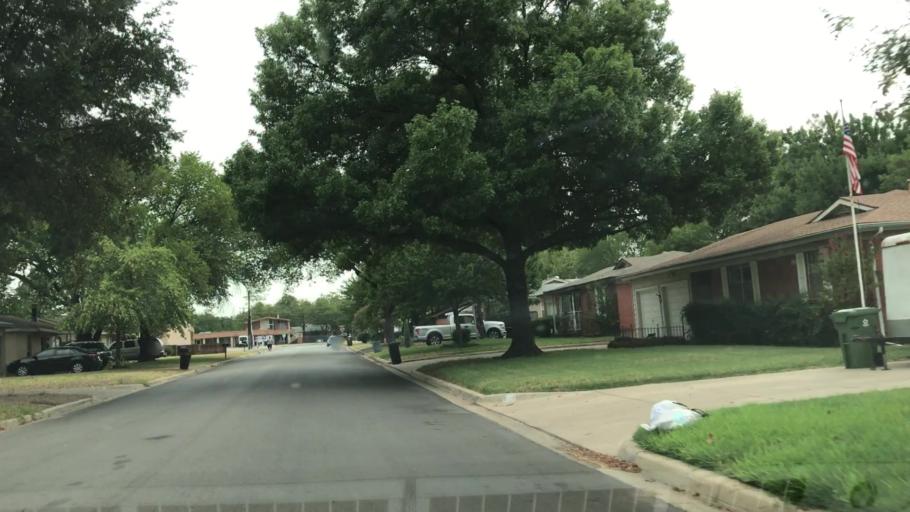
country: US
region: Texas
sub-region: Tarrant County
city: Hurst
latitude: 32.8324
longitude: -97.1697
